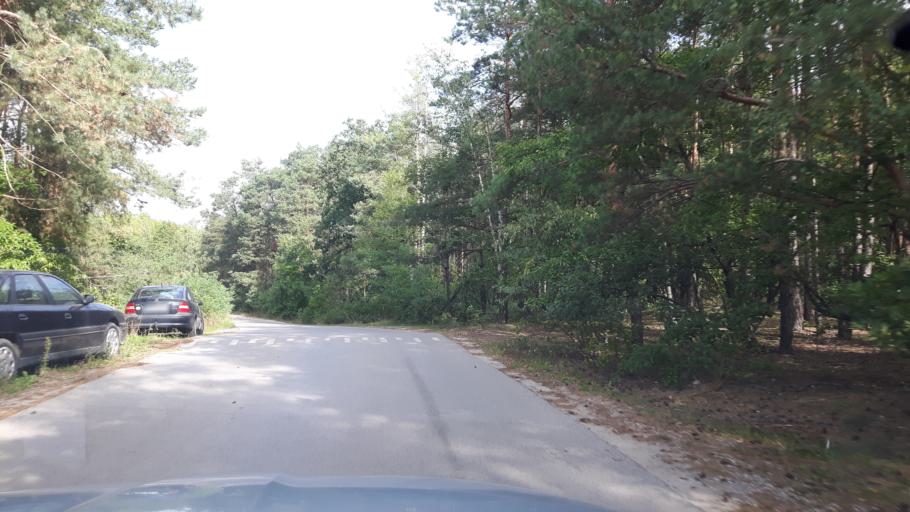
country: PL
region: Masovian Voivodeship
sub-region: Powiat wolominski
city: Marki
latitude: 52.3414
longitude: 21.0814
